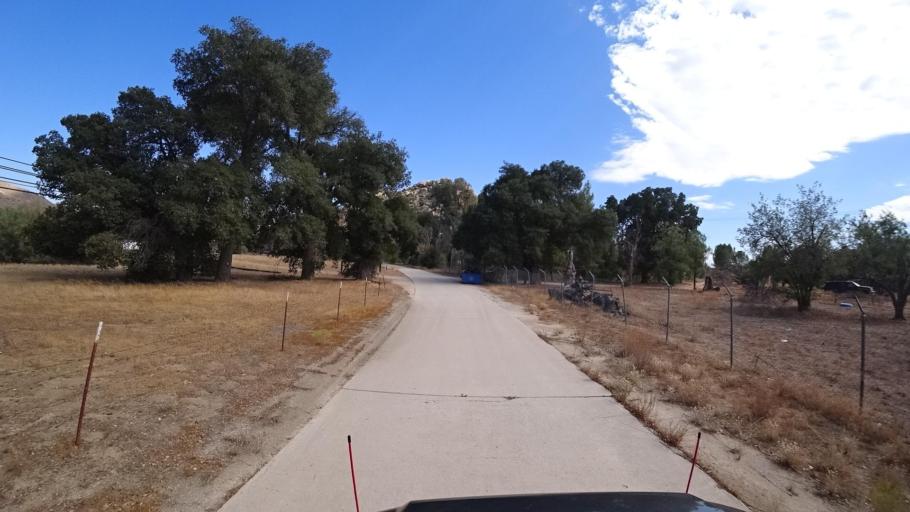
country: MX
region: Baja California
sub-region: Tecate
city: Cereso del Hongo
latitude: 32.6597
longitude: -116.2551
